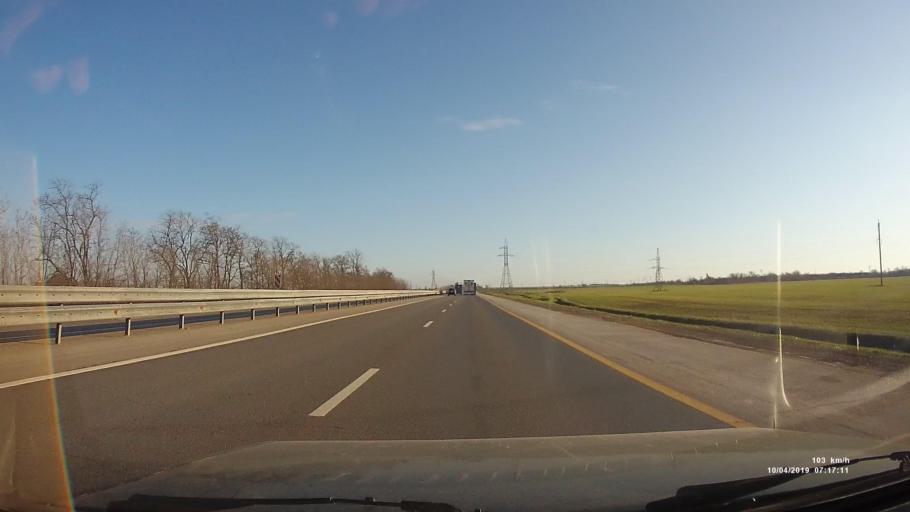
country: RU
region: Rostov
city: Ayutinskiy
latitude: 47.7810
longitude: 40.1617
